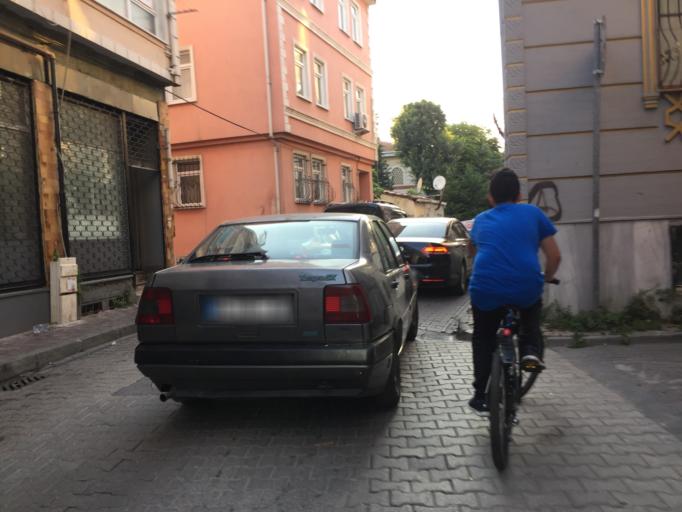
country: TR
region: Istanbul
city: Istanbul
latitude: 41.0225
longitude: 28.9377
